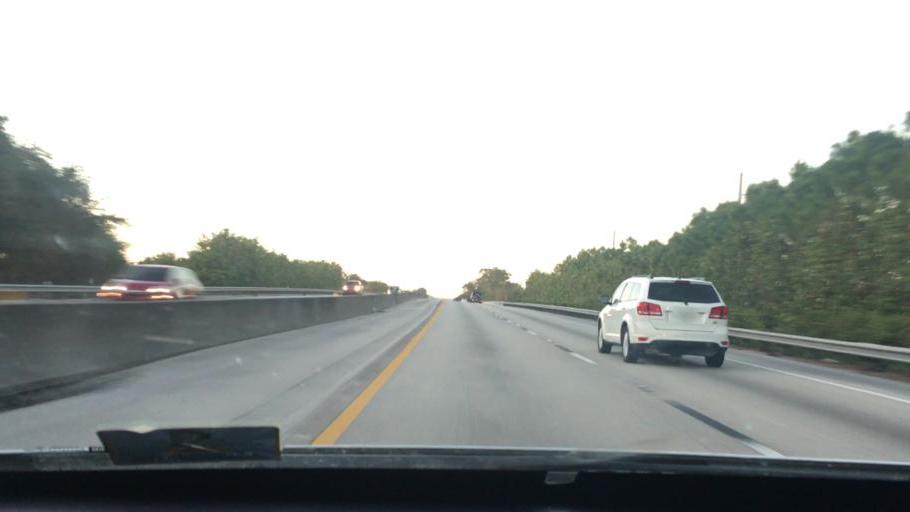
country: US
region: Florida
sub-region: Saint Lucie County
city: Port Saint Lucie
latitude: 27.2610
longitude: -80.3509
